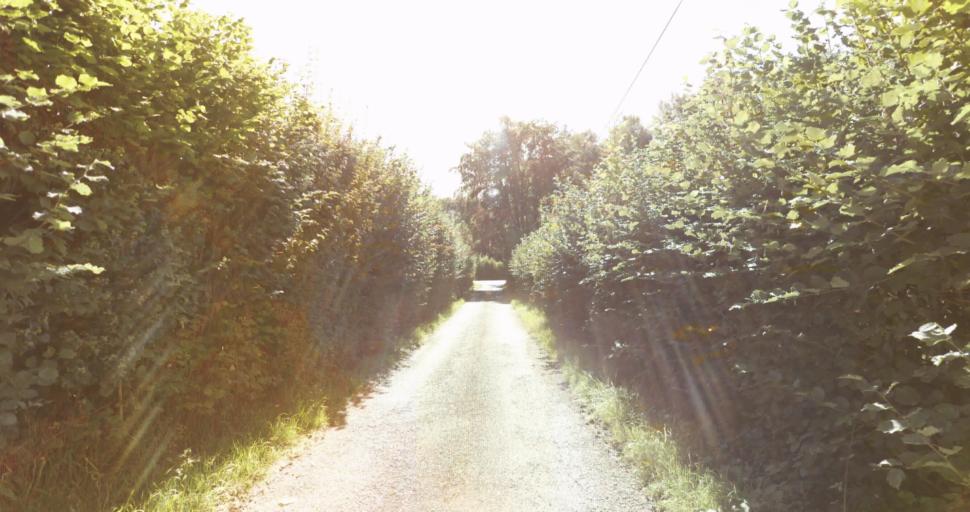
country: FR
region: Lower Normandy
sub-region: Departement de l'Orne
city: Gace
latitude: 48.7666
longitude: 0.2492
